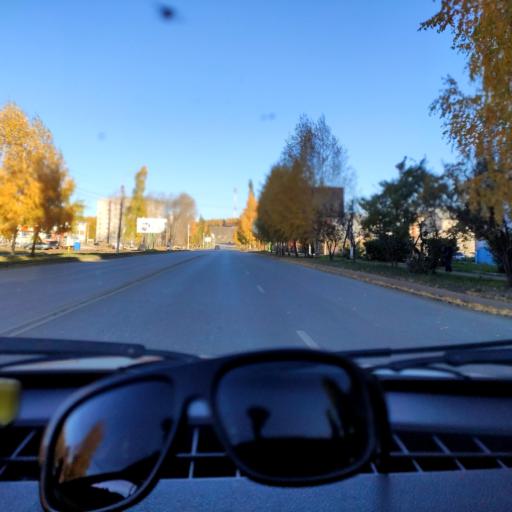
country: RU
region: Bashkortostan
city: Blagoveshchensk
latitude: 55.0517
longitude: 55.9526
